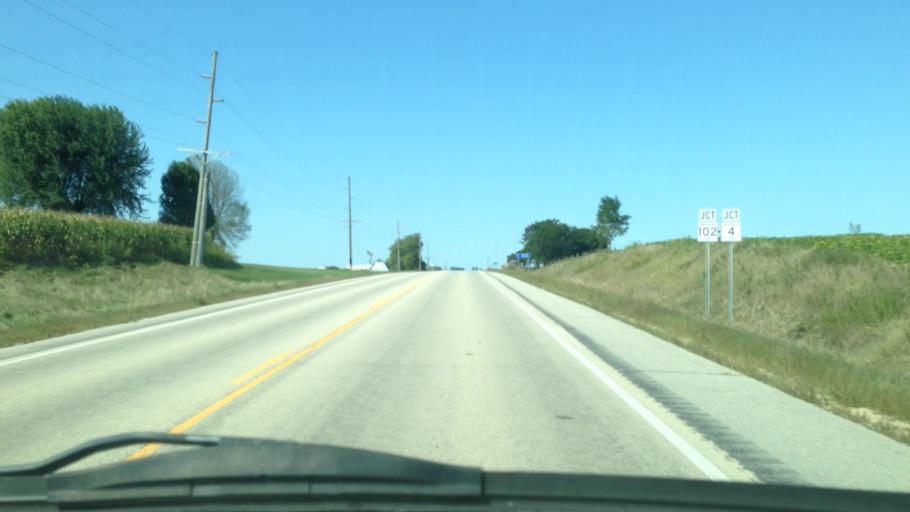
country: US
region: Minnesota
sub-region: Fillmore County
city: Rushford
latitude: 43.8711
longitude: -91.7396
